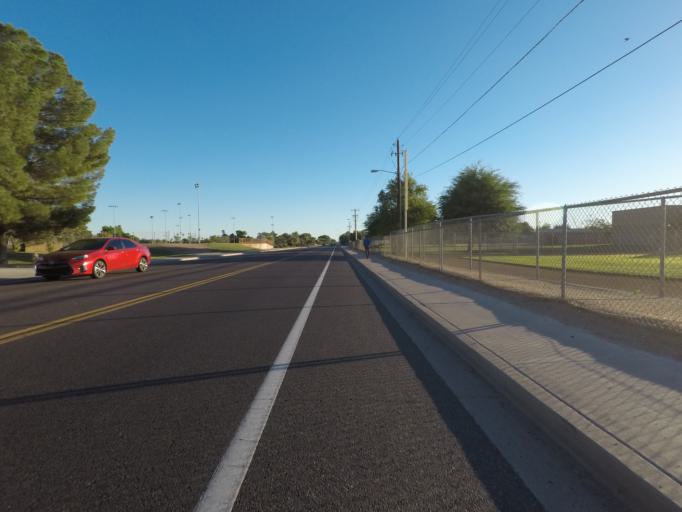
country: US
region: Arizona
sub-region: Maricopa County
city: Scottsdale
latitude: 33.4727
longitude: -111.9176
